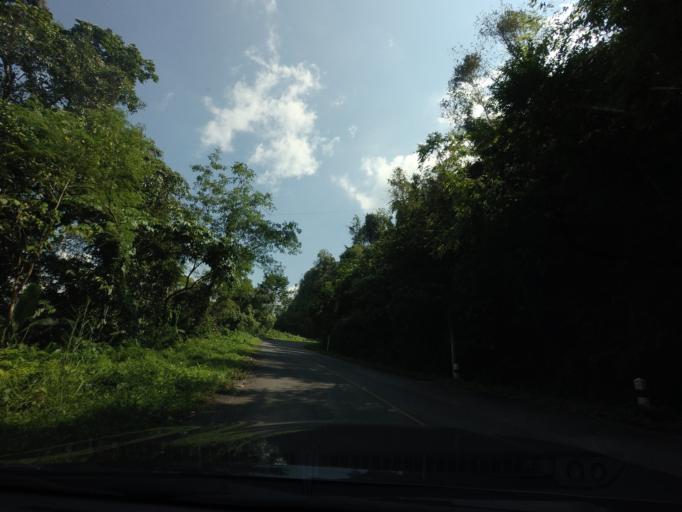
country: TH
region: Nan
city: Bo Kluea
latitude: 19.0591
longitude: 101.0948
